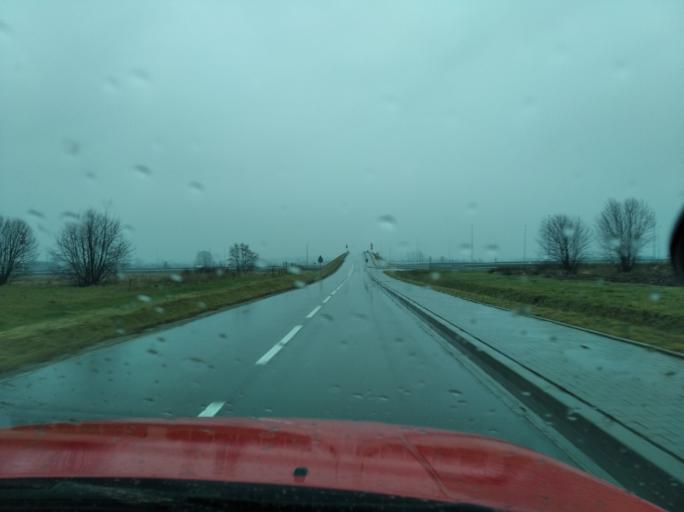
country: PL
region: Subcarpathian Voivodeship
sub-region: Powiat lancucki
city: Czarna
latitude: 50.0925
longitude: 22.1704
